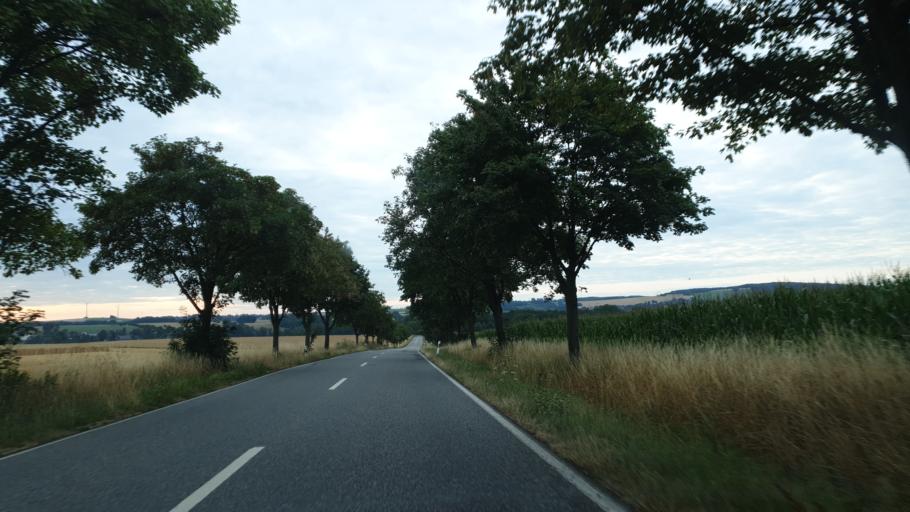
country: DE
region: Saxony
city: Callenberg
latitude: 50.8456
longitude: 12.6628
